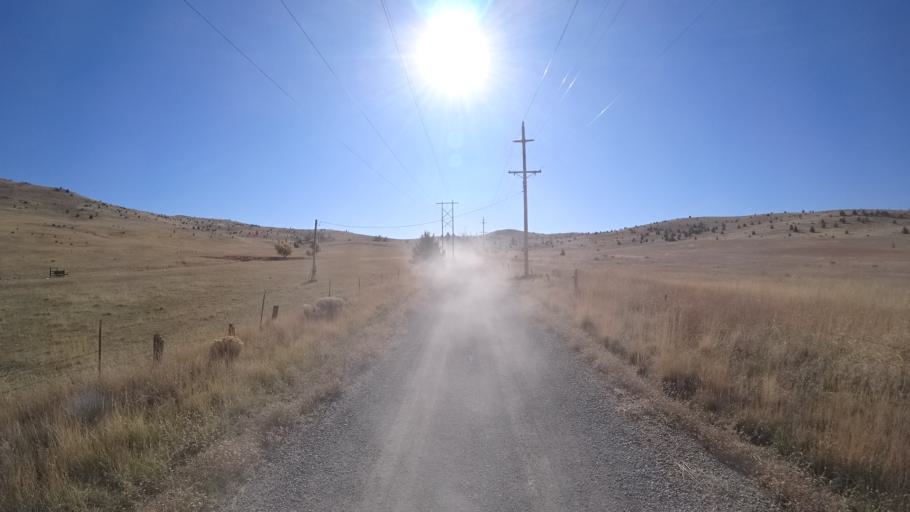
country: US
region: California
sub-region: Siskiyou County
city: Montague
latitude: 41.7825
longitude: -122.3590
